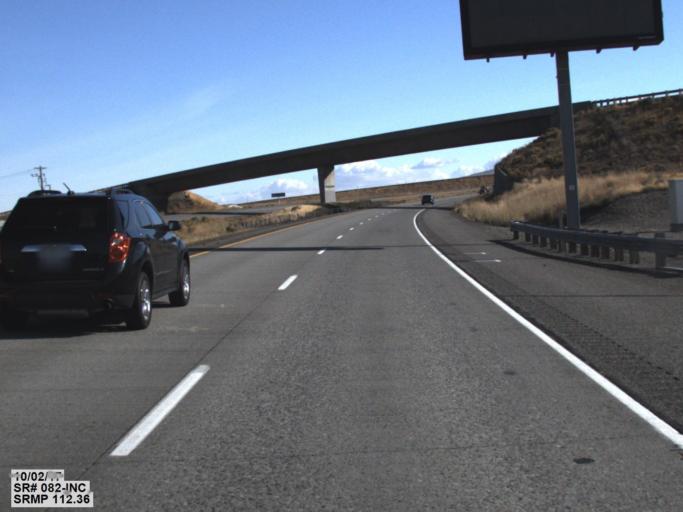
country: US
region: Washington
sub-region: Franklin County
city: West Pasco
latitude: 46.1708
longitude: -119.2073
